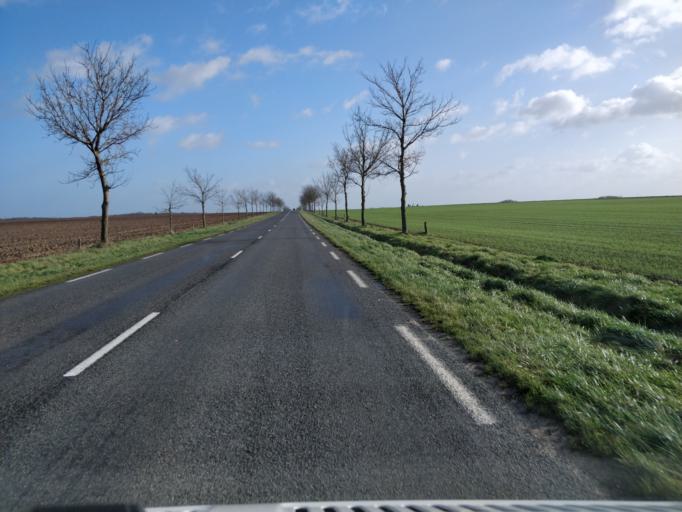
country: FR
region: Ile-de-France
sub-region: Departement de Seine-et-Marne
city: Lorrez-le-Bocage-Preaux
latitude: 48.2105
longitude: 2.9431
